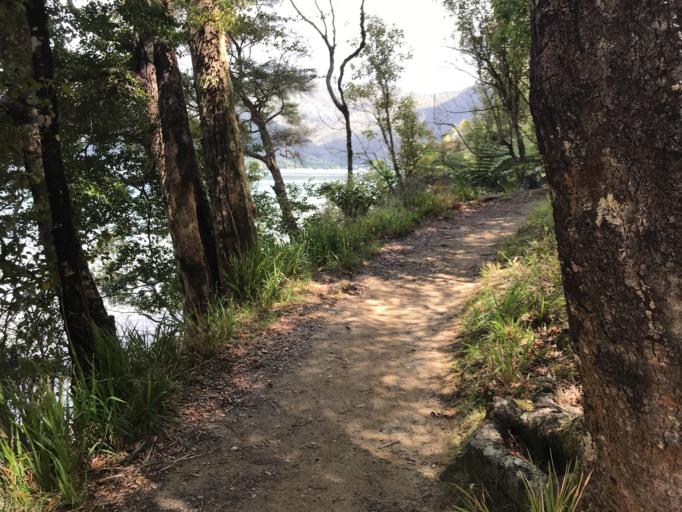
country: NZ
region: Marlborough
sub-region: Marlborough District
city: Picton
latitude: -41.2548
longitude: 173.9391
